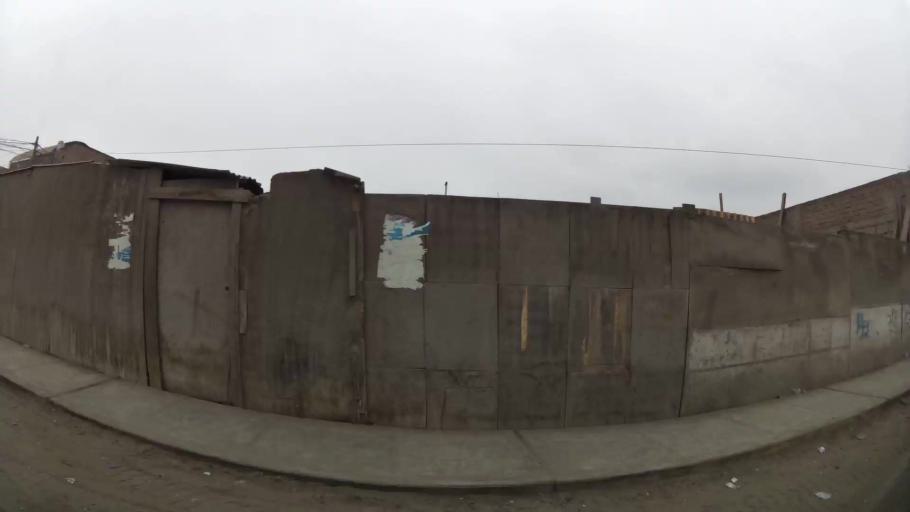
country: PE
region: Lima
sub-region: Lima
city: Surco
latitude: -12.1981
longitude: -76.9628
